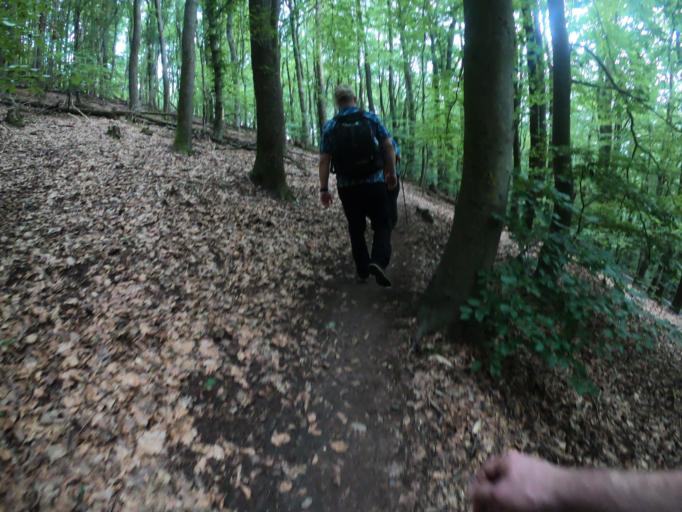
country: DE
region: Rheinland-Pfalz
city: Annweiler am Trifels
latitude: 49.1881
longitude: 7.9872
